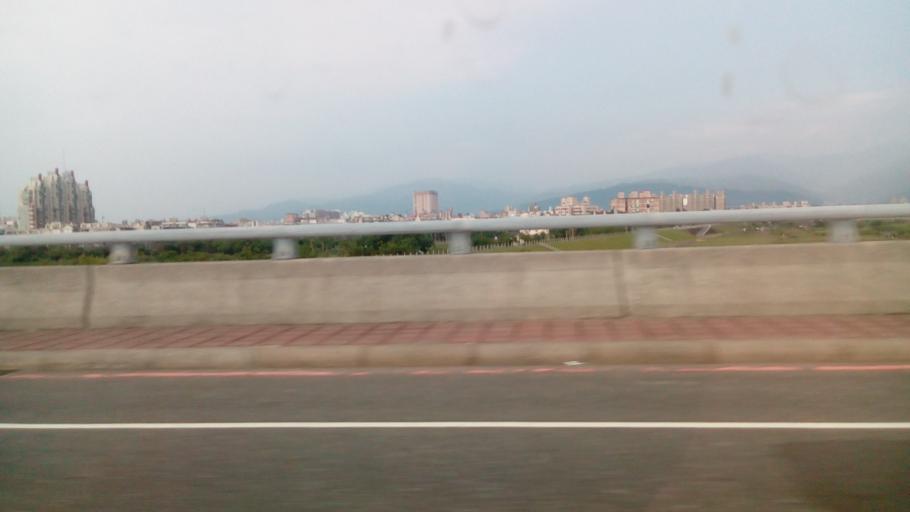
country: TW
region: Taiwan
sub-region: Yilan
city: Yilan
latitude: 24.7604
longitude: 121.7716
